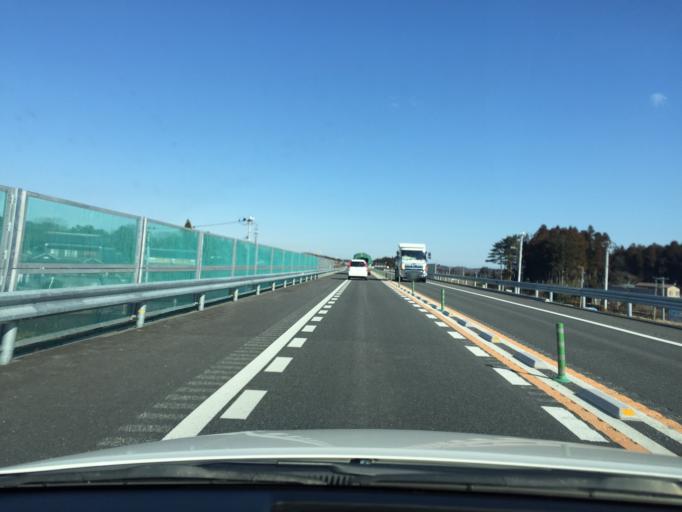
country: JP
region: Fukushima
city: Namie
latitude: 37.6120
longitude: 140.9266
